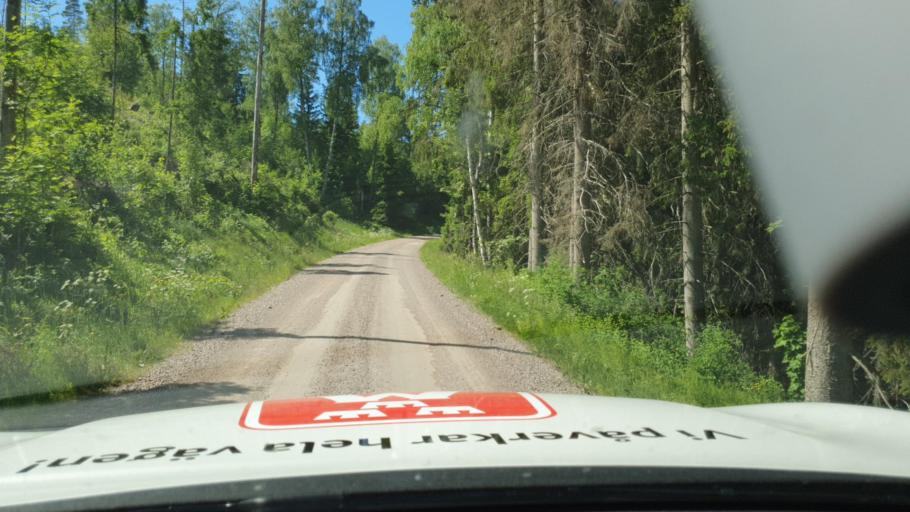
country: SE
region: Joenkoeping
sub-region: Mullsjo Kommun
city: Mullsjoe
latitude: 58.0396
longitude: 13.8618
